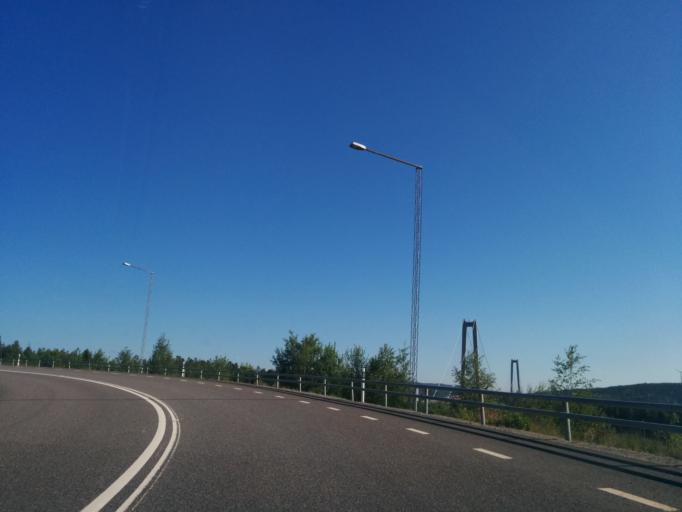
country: SE
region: Vaesternorrland
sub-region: Haernoesands Kommun
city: Haernoesand
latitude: 62.7845
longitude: 17.9205
